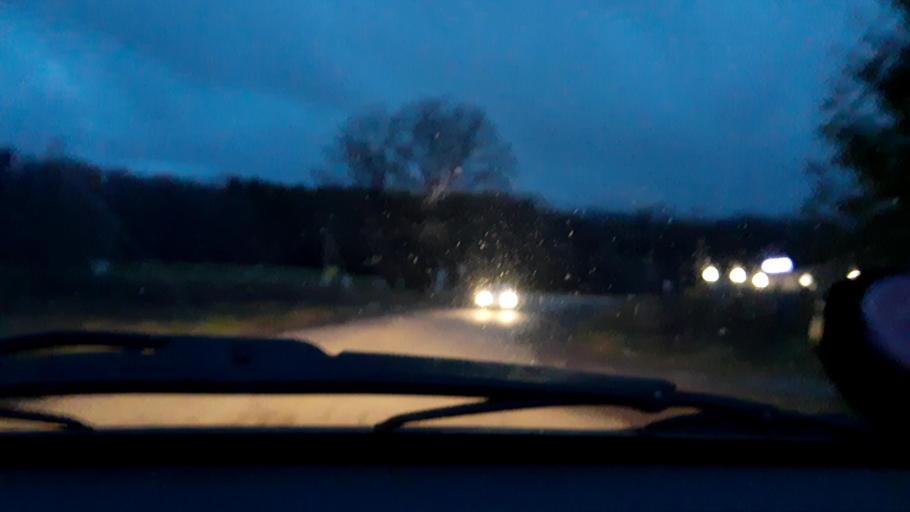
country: RU
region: Bashkortostan
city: Mikhaylovka
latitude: 54.8055
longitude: 55.8774
